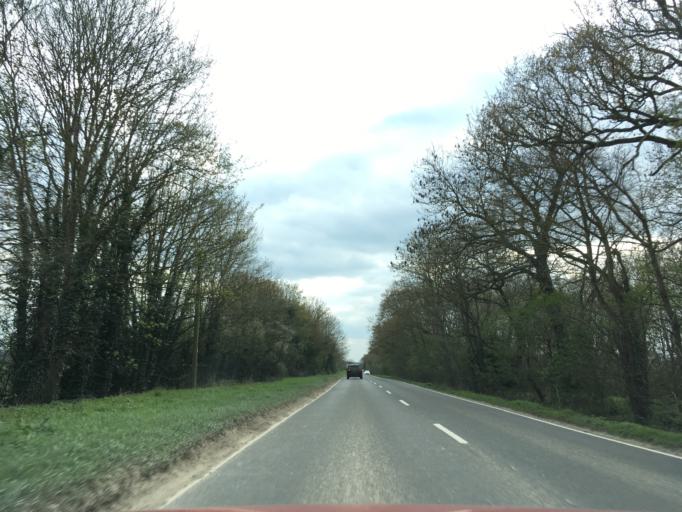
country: GB
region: England
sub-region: Oxfordshire
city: Woodstock
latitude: 51.8420
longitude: -1.3302
